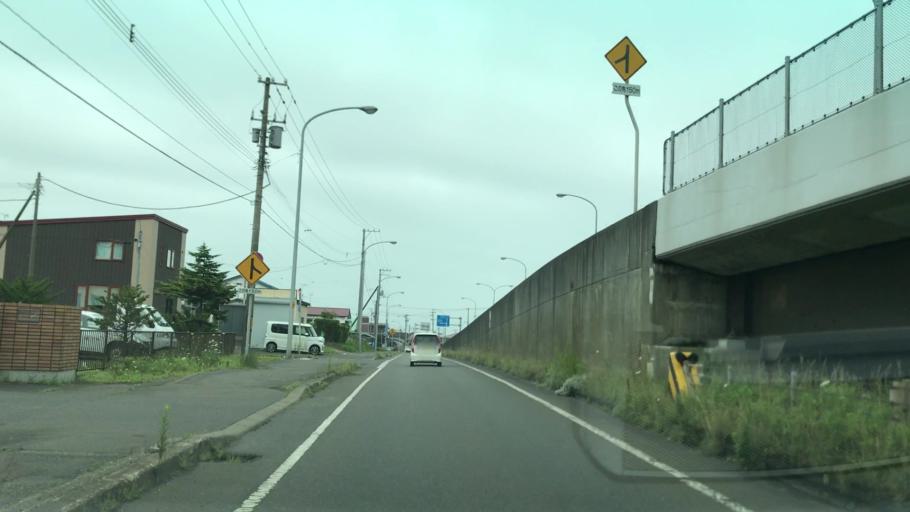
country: JP
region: Hokkaido
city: Muroran
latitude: 42.3532
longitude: 141.0452
